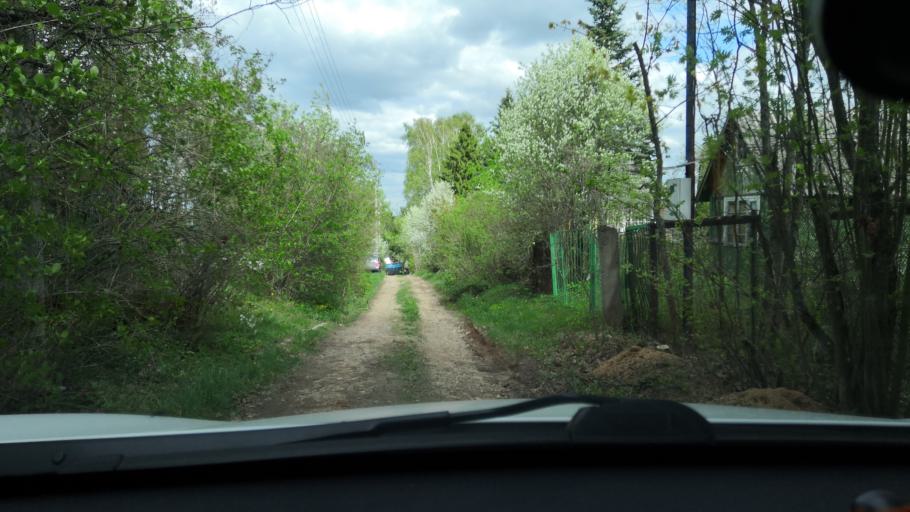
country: RU
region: Moskovskaya
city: Dedenevo
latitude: 56.2636
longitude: 37.5722
